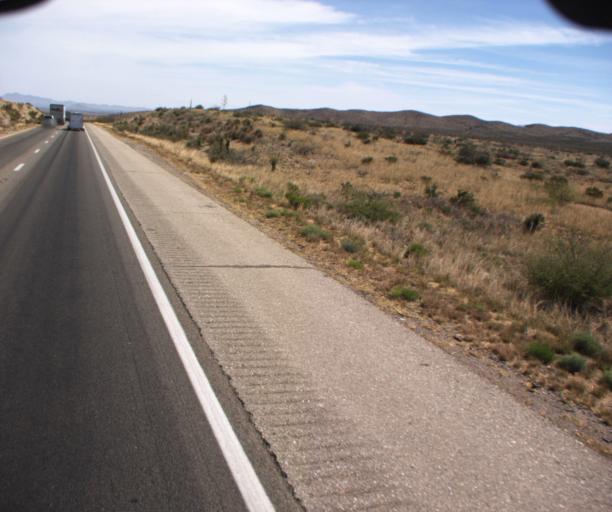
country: US
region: Arizona
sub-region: Cochise County
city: Willcox
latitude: 32.1327
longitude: -110.0070
